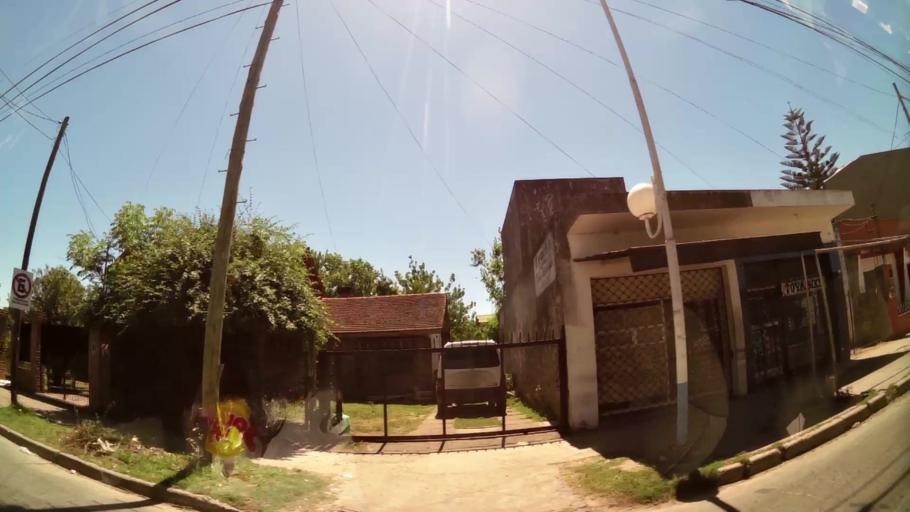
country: AR
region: Buenos Aires
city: Hurlingham
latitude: -34.5044
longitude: -58.6841
